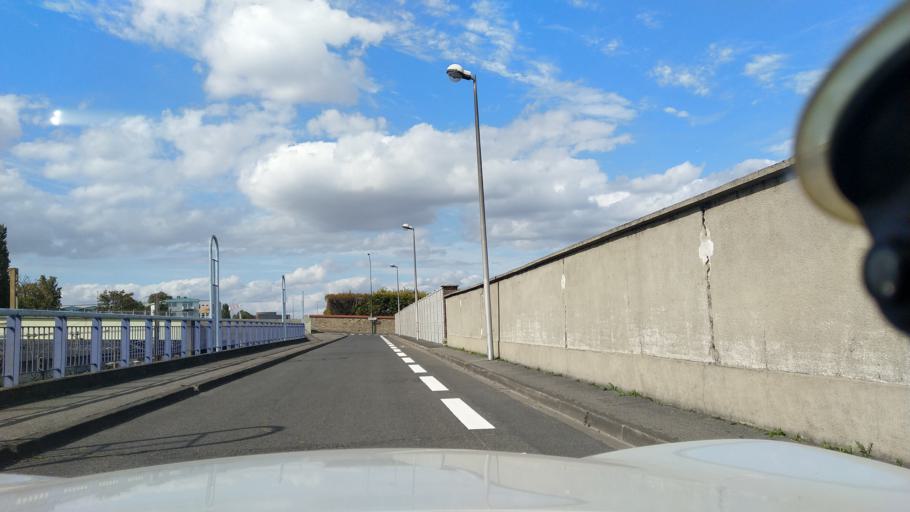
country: FR
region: Ile-de-France
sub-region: Departement du Val-de-Marne
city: Le Perreux-sur-Marne
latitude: 48.8448
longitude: 2.4931
